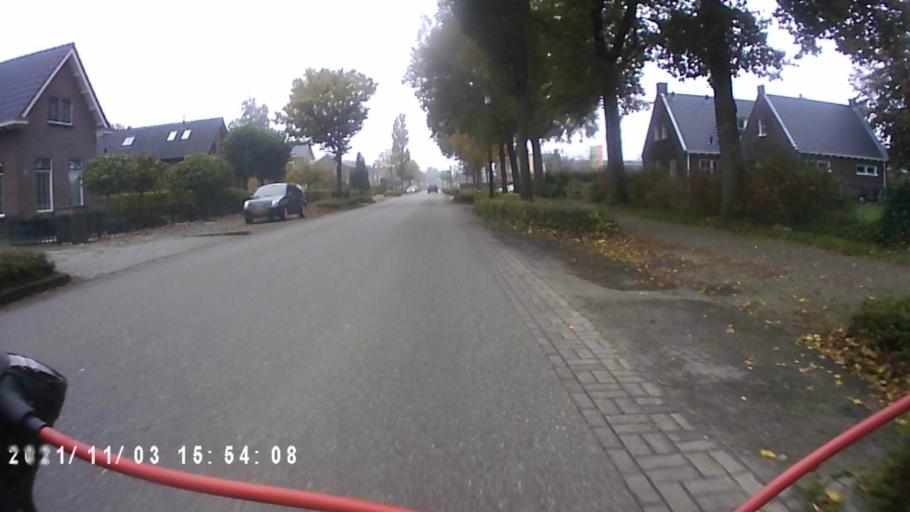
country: NL
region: Groningen
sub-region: Gemeente Leek
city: Leek
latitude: 53.0691
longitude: 6.3320
